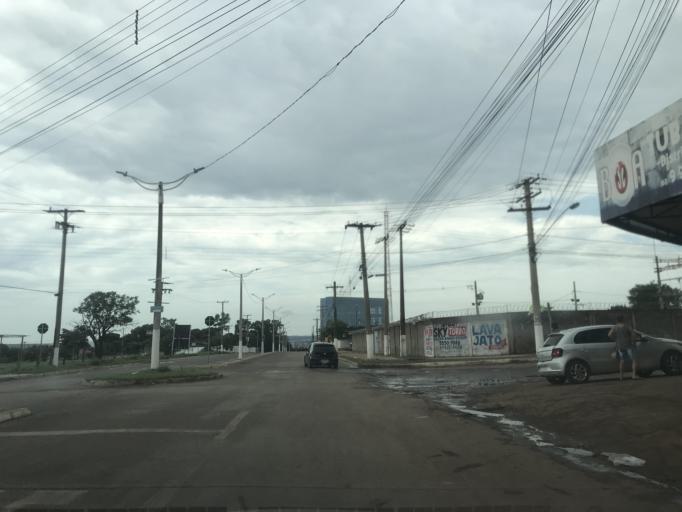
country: BR
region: Goias
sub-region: Luziania
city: Luziania
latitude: -16.2382
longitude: -47.9427
